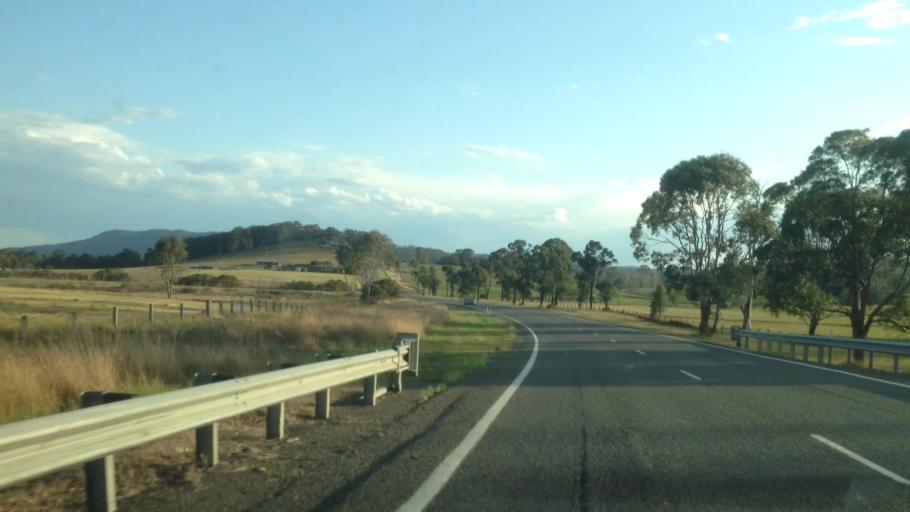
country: AU
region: New South Wales
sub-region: Cessnock
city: Kurri Kurri
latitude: -32.8745
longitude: 151.4758
